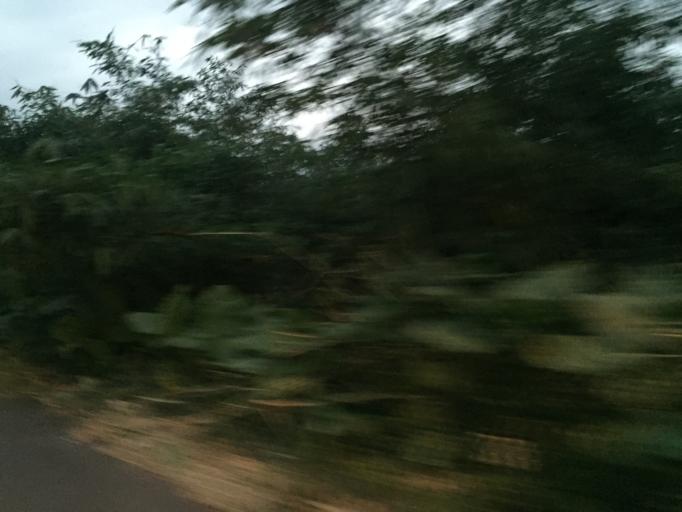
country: TW
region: Taiwan
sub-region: Yilan
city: Yilan
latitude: 24.7600
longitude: 121.7386
